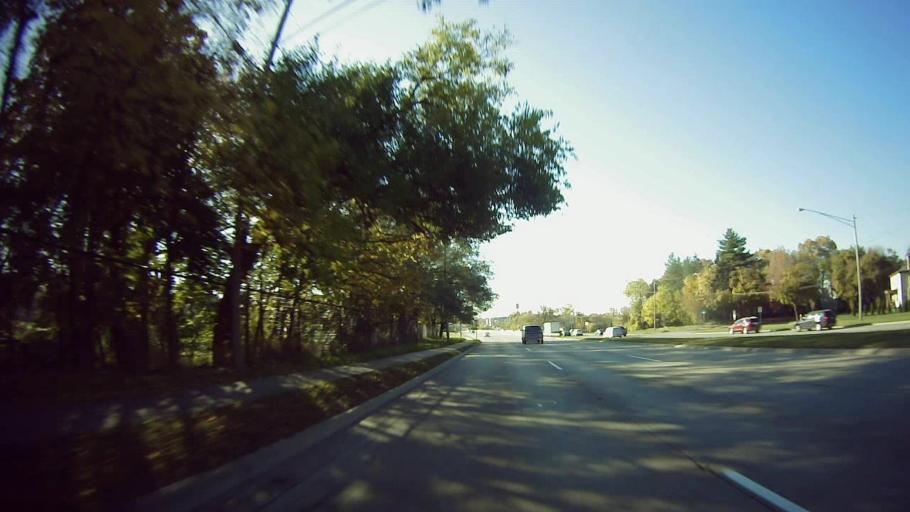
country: US
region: Michigan
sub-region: Wayne County
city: Dearborn Heights
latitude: 42.3038
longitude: -83.2719
